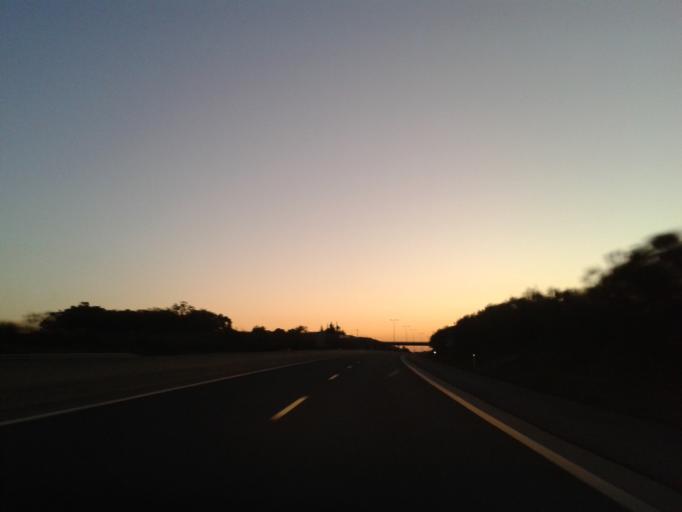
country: PT
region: Faro
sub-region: Albufeira
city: Guia
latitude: 37.1394
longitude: -8.3323
